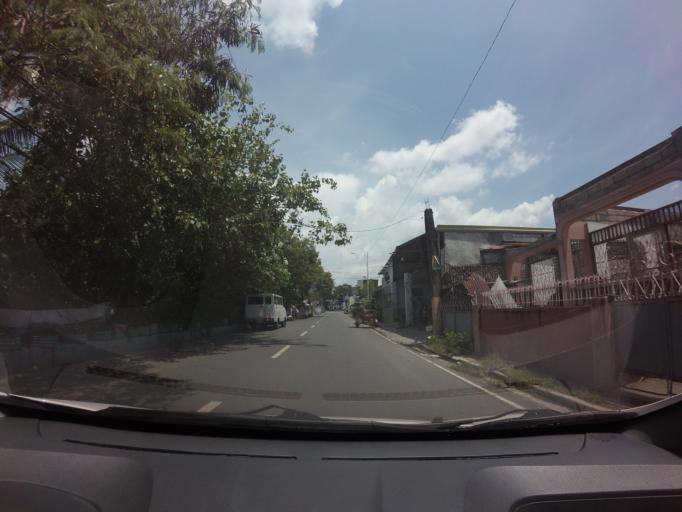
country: PH
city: Sambayanihan People's Village
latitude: 14.4262
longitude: 121.0147
